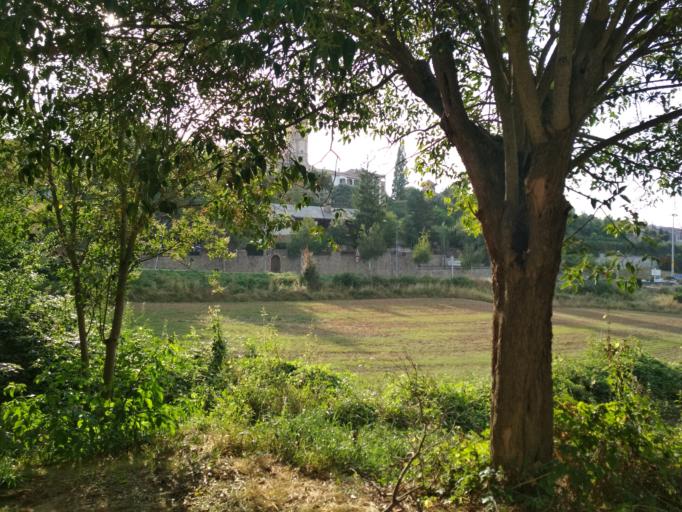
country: ES
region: Catalonia
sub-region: Provincia de Barcelona
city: Castelltercol
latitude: 41.7512
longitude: 2.1237
